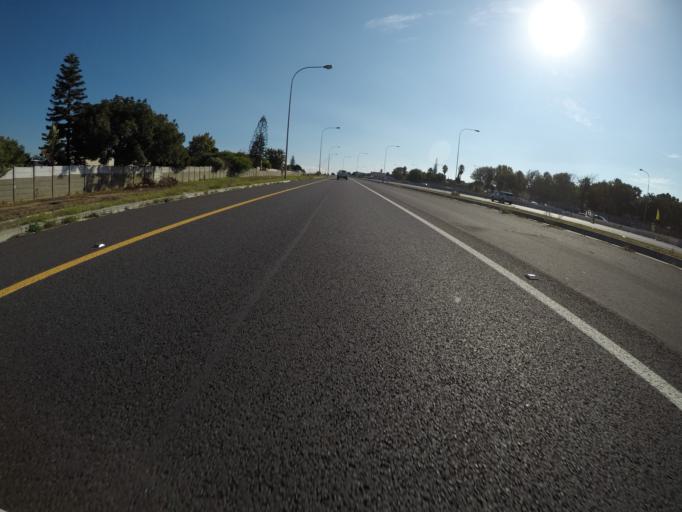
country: ZA
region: Western Cape
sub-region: City of Cape Town
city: Kraaifontein
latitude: -33.8743
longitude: 18.6659
